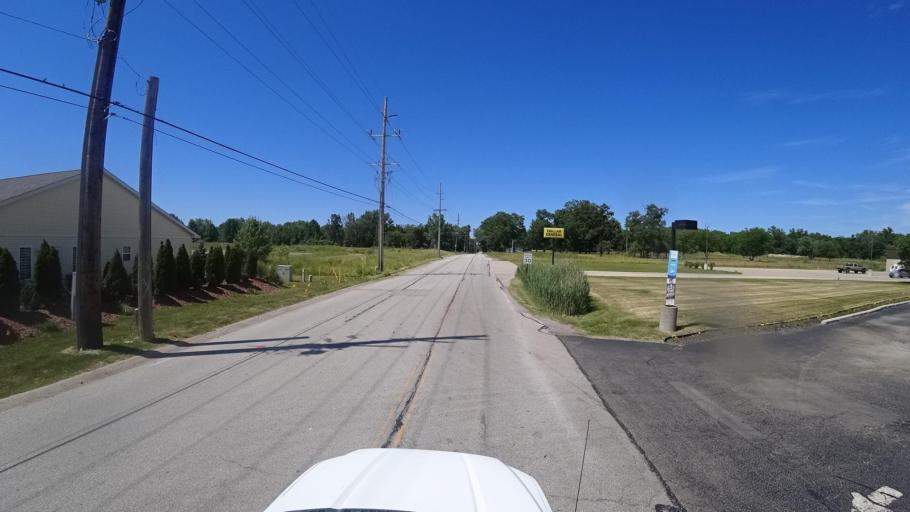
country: US
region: Indiana
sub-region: Porter County
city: Porter
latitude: 41.6325
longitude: -87.0673
